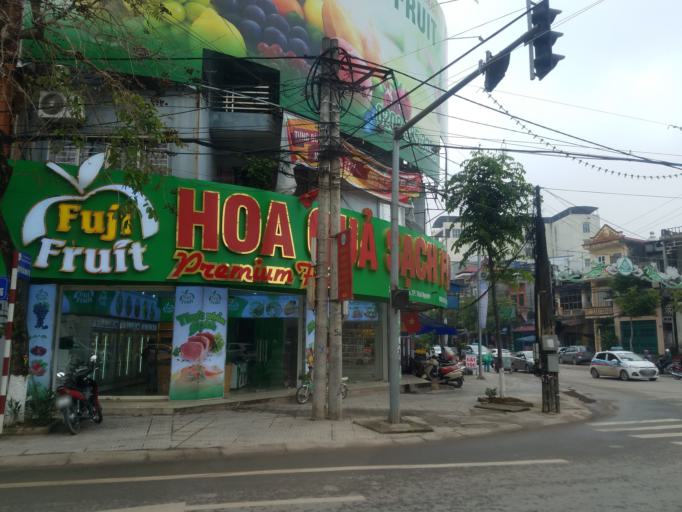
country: VN
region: Thai Nguyen
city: Thanh Pho Thai Nguyen
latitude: 21.5860
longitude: 105.8409
